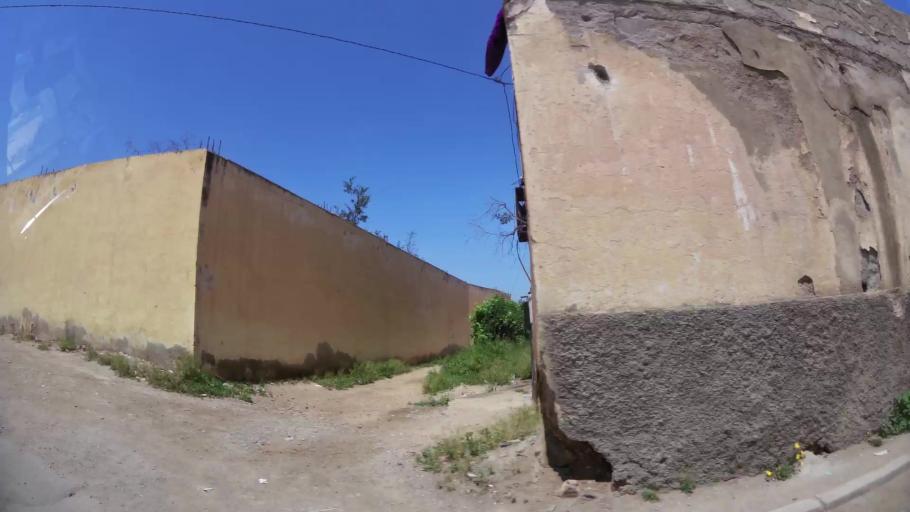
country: MA
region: Oriental
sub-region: Oujda-Angad
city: Oujda
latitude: 34.6863
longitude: -1.8989
